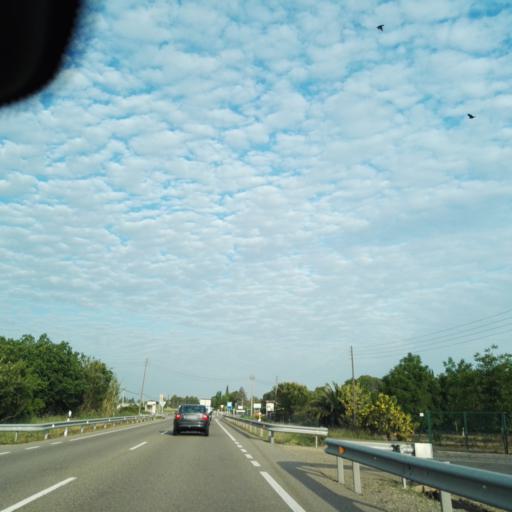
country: ES
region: Aragon
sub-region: Provincia de Zaragoza
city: Oliver-Valdefierro, Oliver, Valdefierro
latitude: 41.6637
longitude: -0.9745
